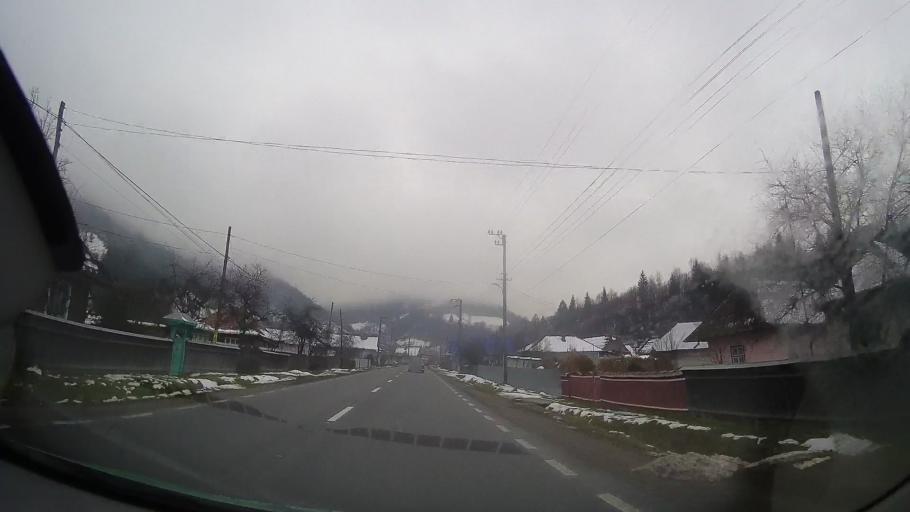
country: RO
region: Neamt
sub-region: Comuna Bicazu Ardelean
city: Bicazu Ardelean
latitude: 46.8591
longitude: 25.9366
